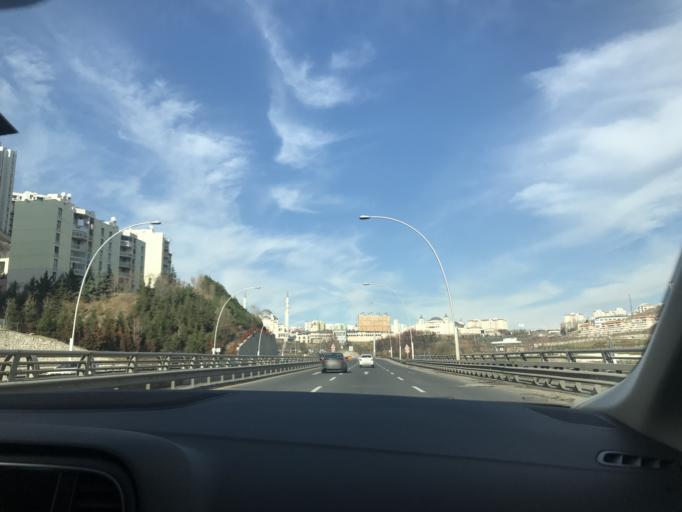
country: TR
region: Ankara
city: Mamak
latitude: 40.0001
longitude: 32.8946
